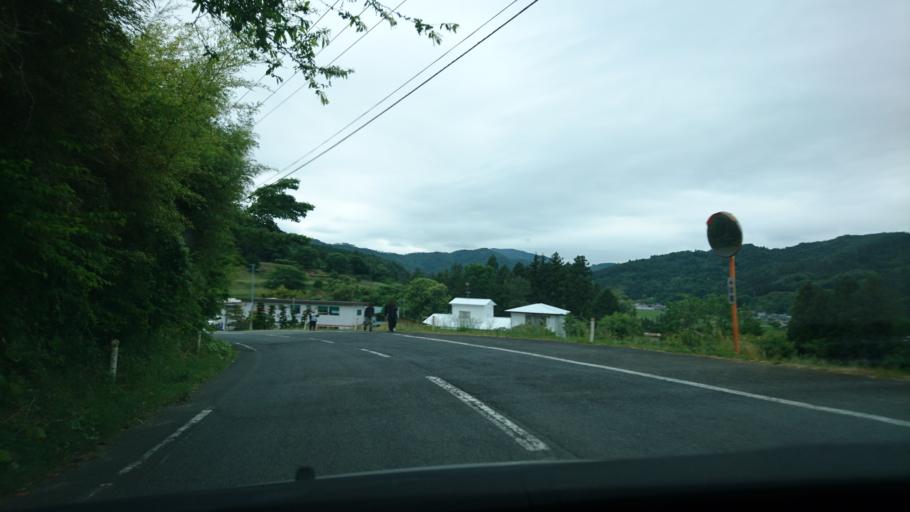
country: JP
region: Iwate
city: Ichinoseki
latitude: 38.9524
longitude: 141.2565
